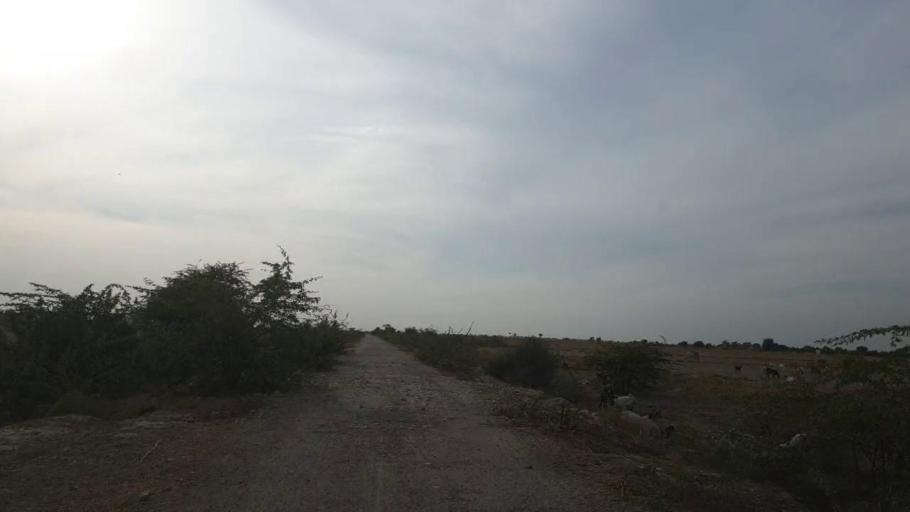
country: PK
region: Sindh
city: Nabisar
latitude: 24.9974
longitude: 69.5246
